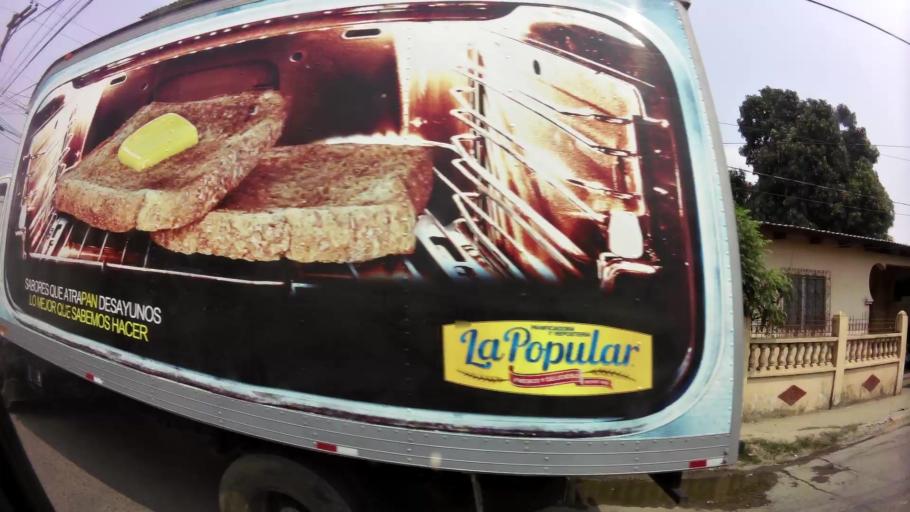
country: HN
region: Cortes
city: La Lima
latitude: 15.4386
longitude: -87.9252
